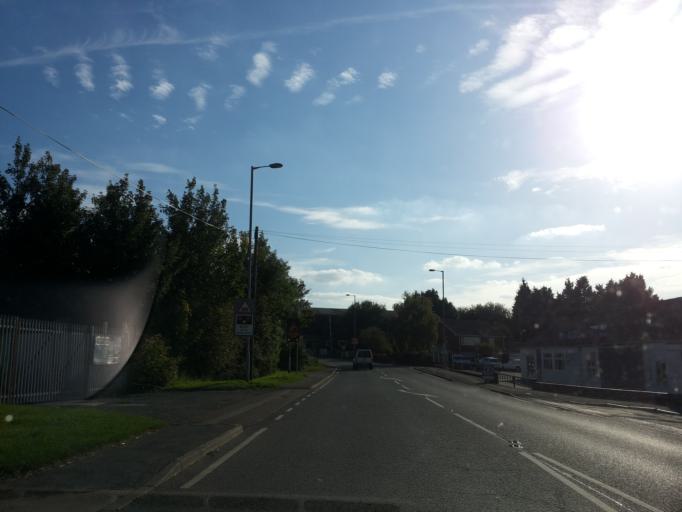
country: GB
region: England
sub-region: East Riding of Yorkshire
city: Snaith
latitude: 53.6940
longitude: -1.0285
